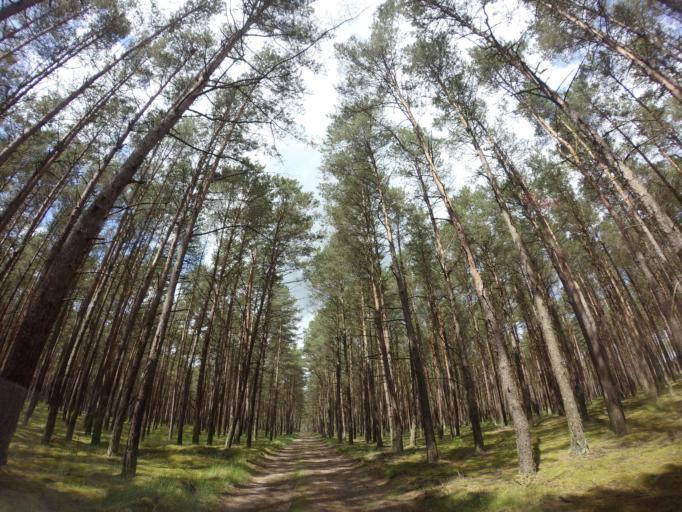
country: PL
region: West Pomeranian Voivodeship
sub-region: Powiat drawski
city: Kalisz Pomorski
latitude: 53.1864
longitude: 15.9124
